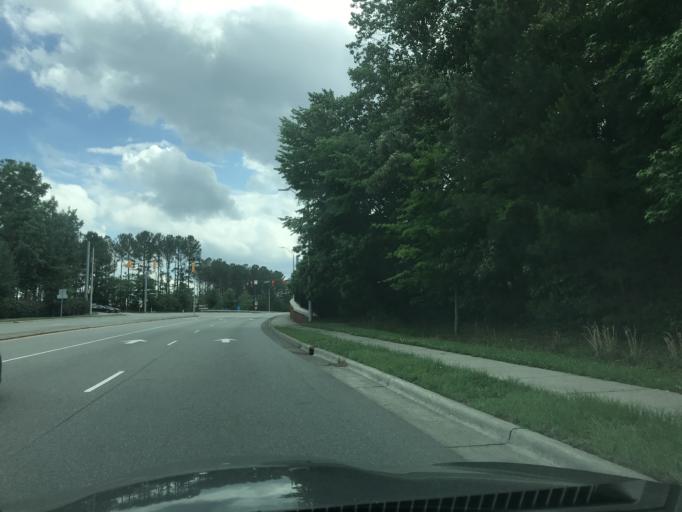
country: US
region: North Carolina
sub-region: Wake County
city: Wake Forest
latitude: 35.9270
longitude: -78.5876
